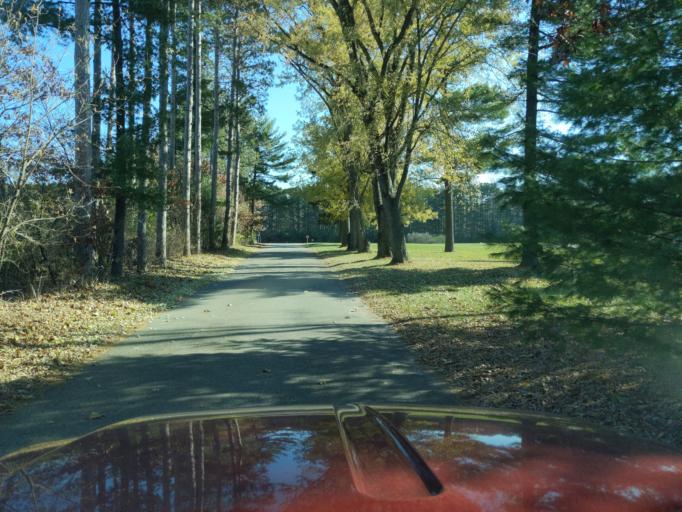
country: US
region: Wisconsin
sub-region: Waushara County
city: Wautoma
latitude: 44.0332
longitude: -89.2999
